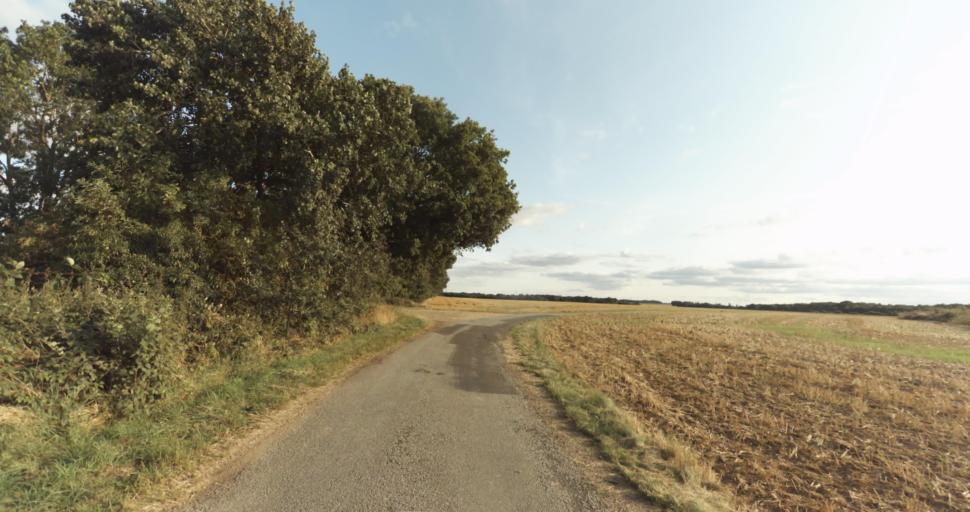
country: FR
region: Haute-Normandie
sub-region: Departement de l'Eure
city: Marcilly-sur-Eure
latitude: 48.8872
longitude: 1.2776
